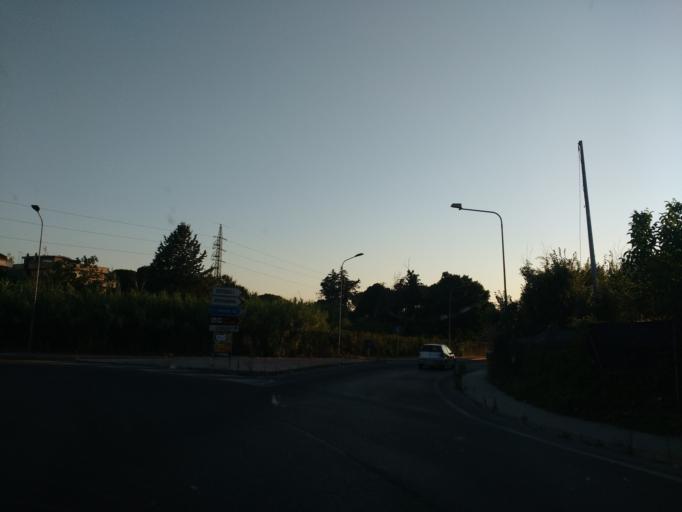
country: IT
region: Latium
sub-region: Citta metropolitana di Roma Capitale
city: Albuccione
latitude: 41.9523
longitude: 12.6970
